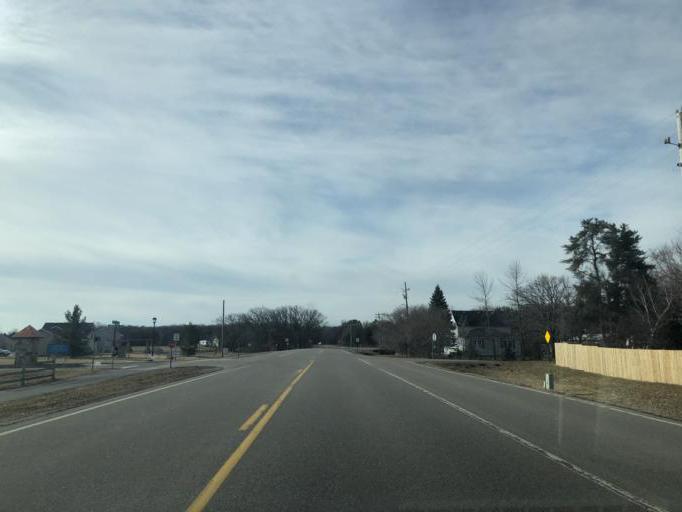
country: US
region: Minnesota
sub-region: Sherburne County
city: Becker
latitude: 45.3977
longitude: -93.8498
